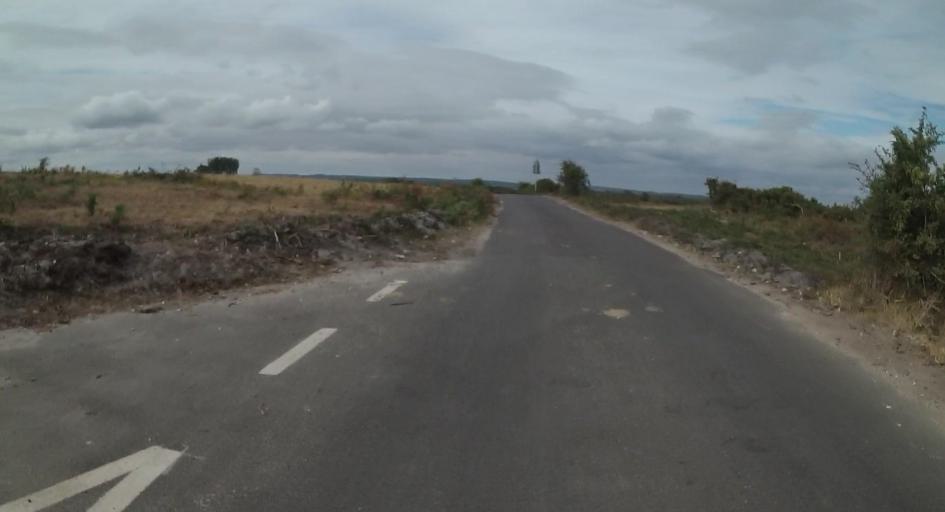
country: GB
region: England
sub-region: Dorset
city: Wareham
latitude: 50.6593
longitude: -2.0864
